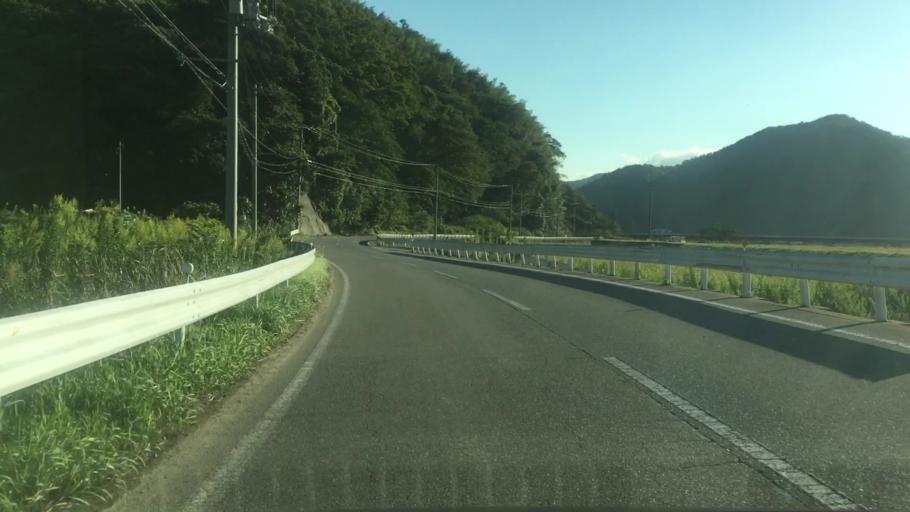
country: JP
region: Hyogo
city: Toyooka
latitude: 35.6103
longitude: 134.8088
